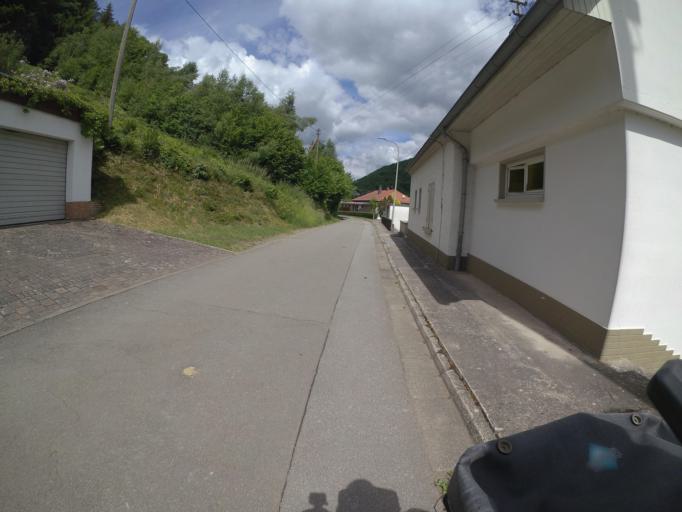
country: DE
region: Rheinland-Pfalz
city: Fockelberg
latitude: 49.5403
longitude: 7.4968
